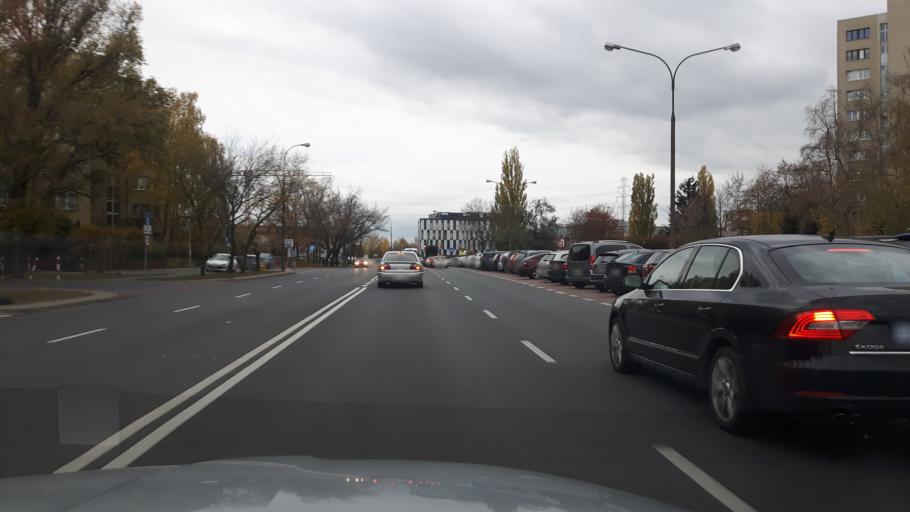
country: PL
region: Masovian Voivodeship
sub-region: Warszawa
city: Ursynow
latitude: 52.1524
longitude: 21.0287
